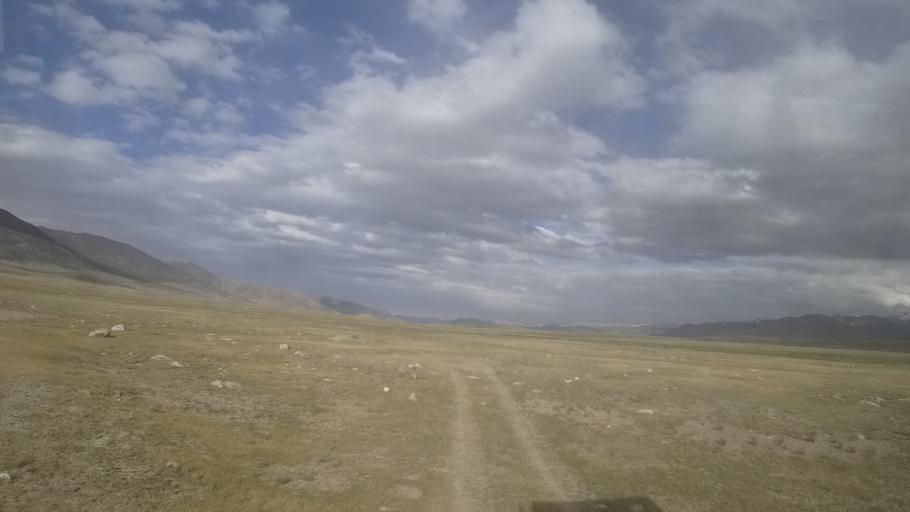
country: TJ
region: Gorno-Badakhshan
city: Murghob
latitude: 37.4689
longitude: 73.9350
